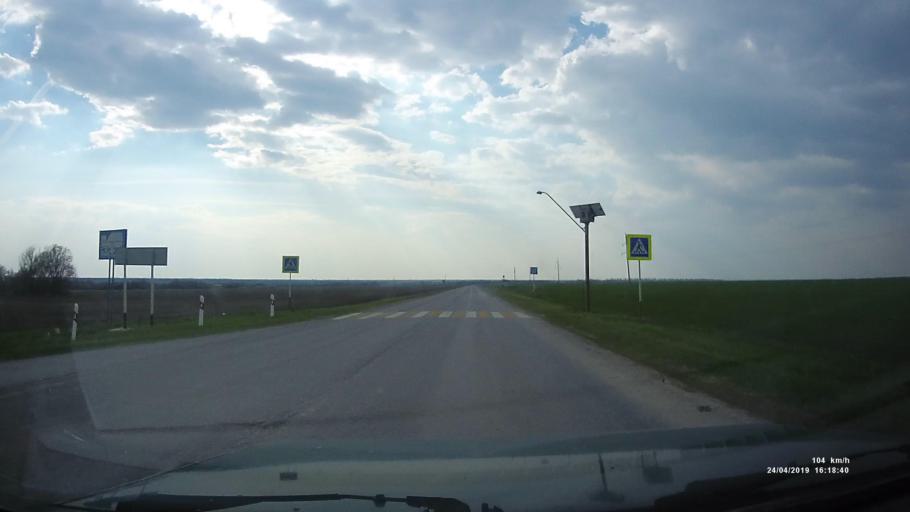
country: RU
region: Rostov
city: Sovetskoye
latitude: 46.7757
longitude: 42.1116
